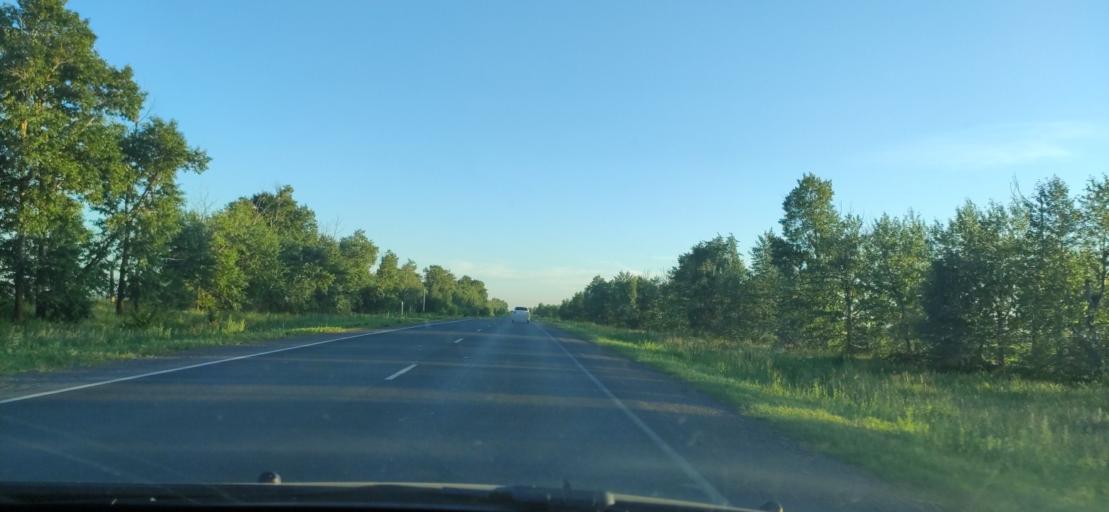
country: RU
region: Ulyanovsk
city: Cherdakly
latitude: 54.4055
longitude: 48.8695
